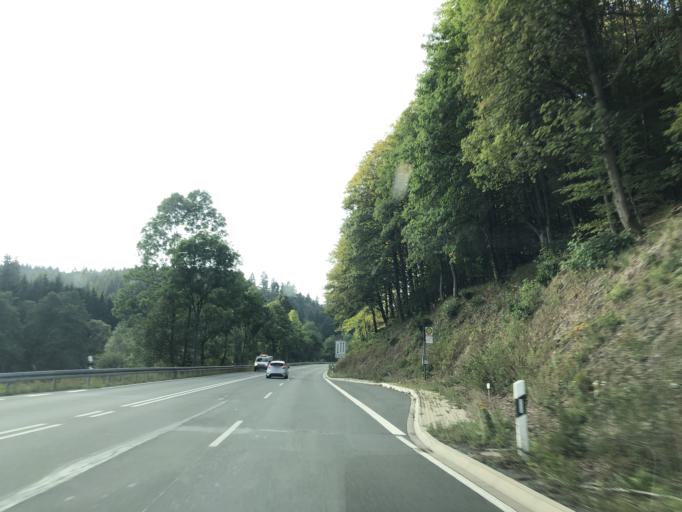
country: DE
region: North Rhine-Westphalia
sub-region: Regierungsbezirk Arnsberg
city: Winterberg
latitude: 51.1786
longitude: 8.5290
